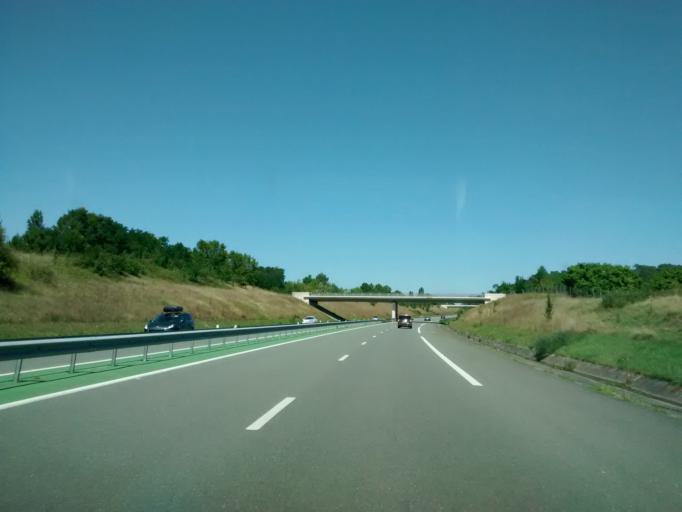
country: FR
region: Aquitaine
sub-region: Departement de la Dordogne
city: Neuvic
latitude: 45.0906
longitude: 0.4731
